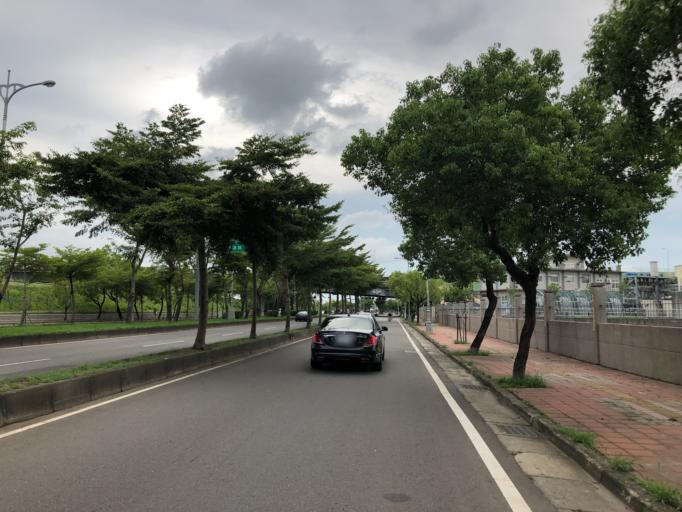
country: TW
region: Taiwan
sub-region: Taichung City
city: Taichung
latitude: 24.0915
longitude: 120.6503
